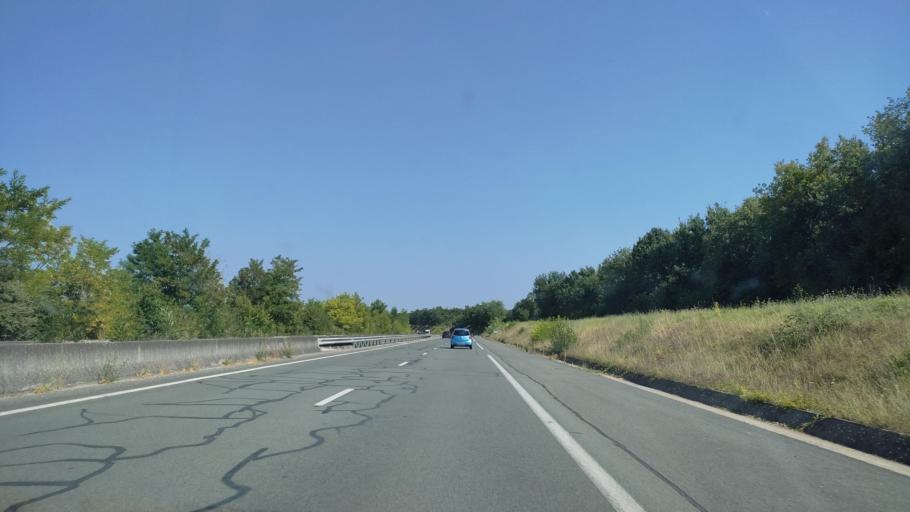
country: FR
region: Poitou-Charentes
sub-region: Departement de la Charente
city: Saint-Yrieix-sur-Charente
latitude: 45.6822
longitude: 0.1200
